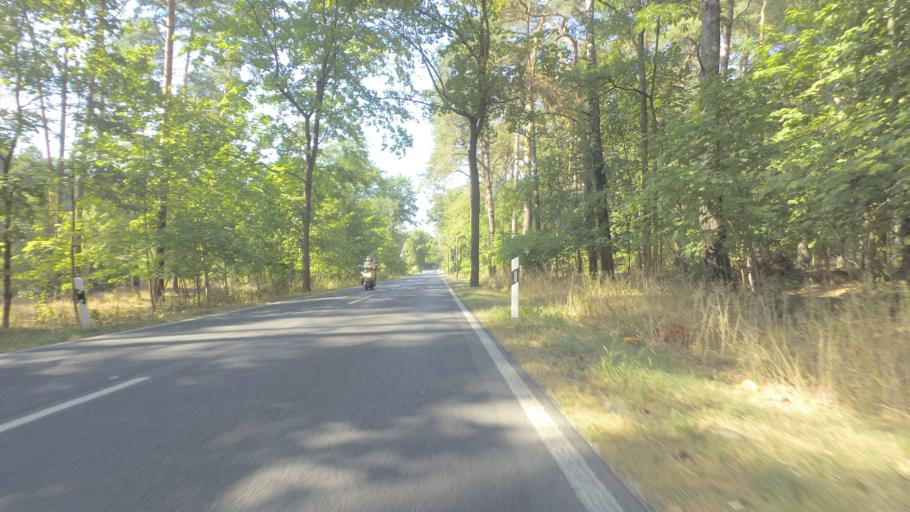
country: DE
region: Brandenburg
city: Rangsdorf
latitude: 52.2604
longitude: 13.3703
